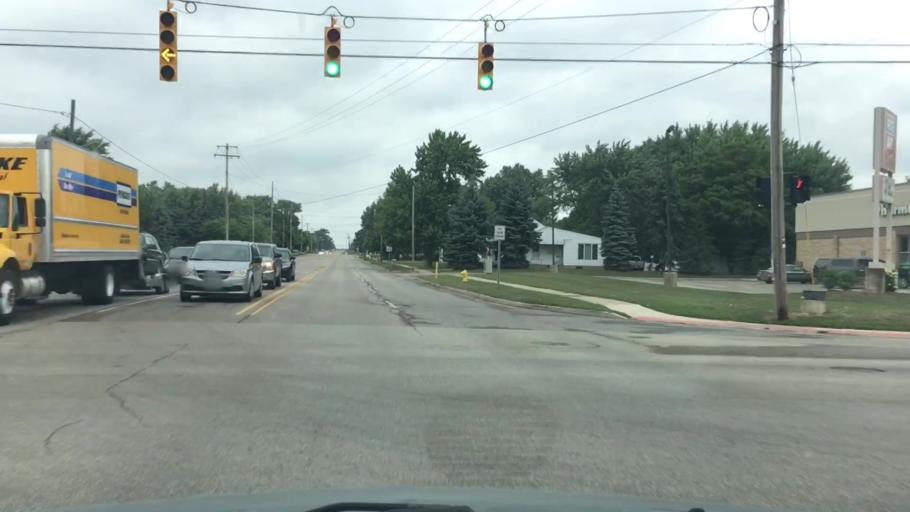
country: US
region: Michigan
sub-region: Ottawa County
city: Hudsonville
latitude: 42.8877
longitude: -85.8519
